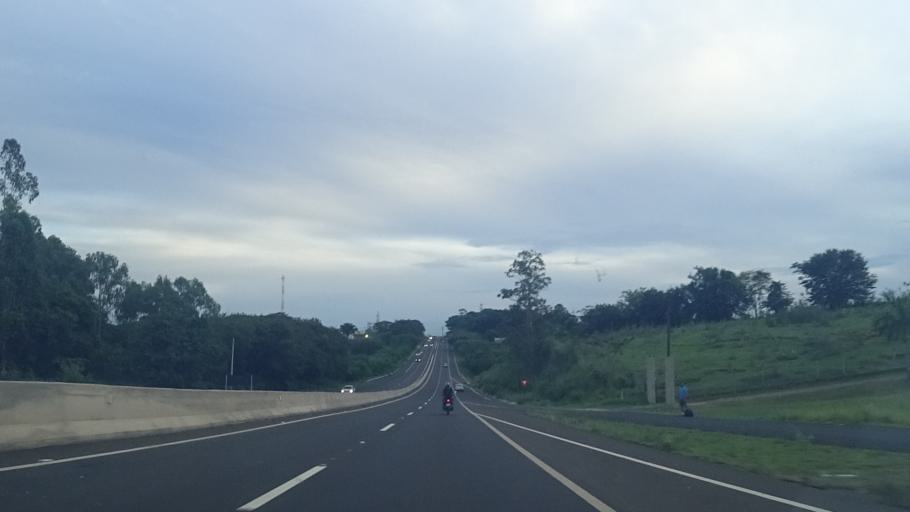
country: BR
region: Sao Paulo
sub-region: Presidente Prudente
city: Presidente Prudente
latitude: -22.1642
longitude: -51.3975
